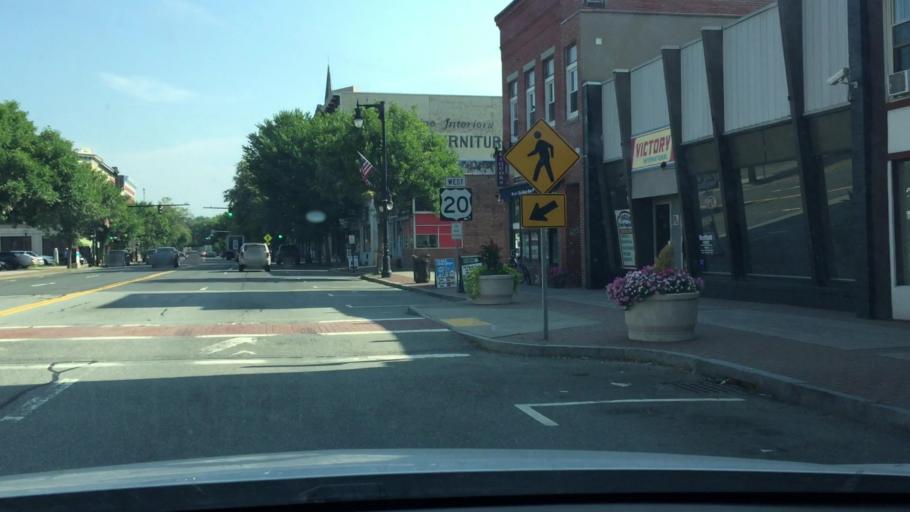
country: US
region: Massachusetts
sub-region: Hampden County
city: Westfield
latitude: 42.1217
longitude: -72.7489
